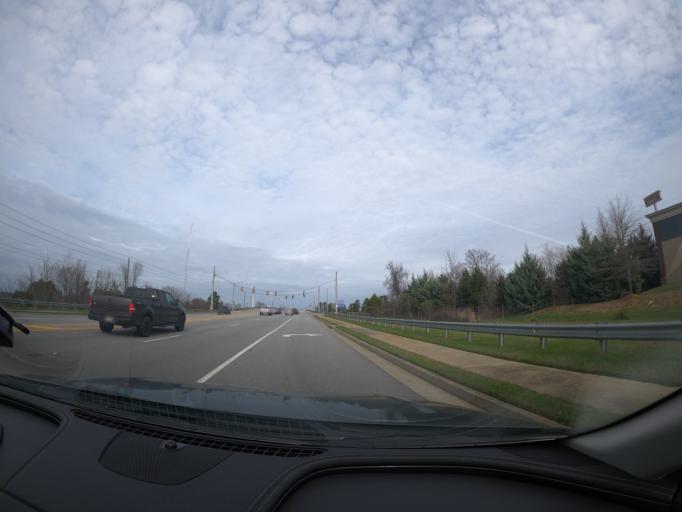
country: US
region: Georgia
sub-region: Columbia County
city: Grovetown
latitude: 33.4818
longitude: -82.1985
